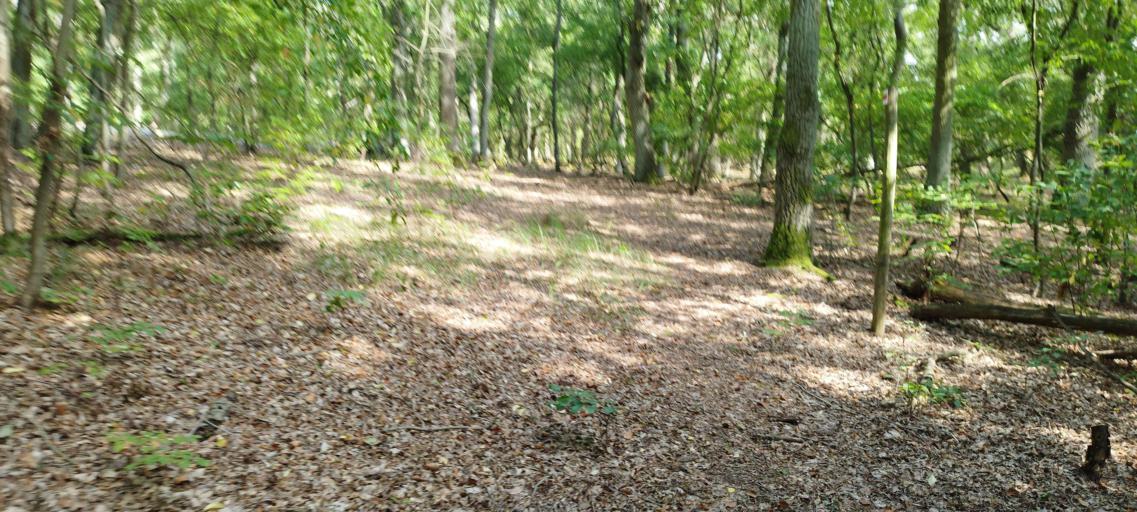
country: DE
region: Brandenburg
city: Nennhausen
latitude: 52.5958
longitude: 12.4249
